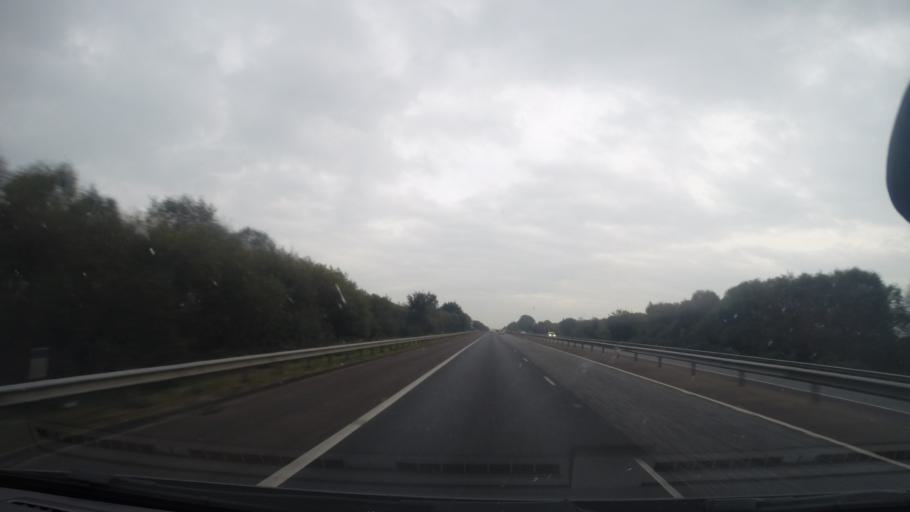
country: GB
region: Northern Ireland
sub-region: Armagh District
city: Portadown
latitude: 54.4744
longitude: -6.4755
